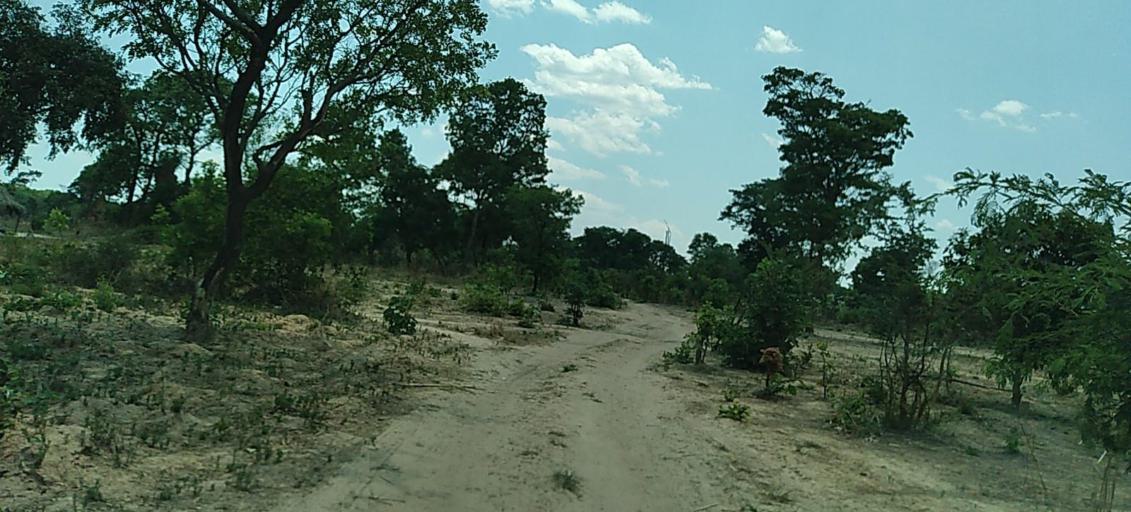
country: ZM
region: Central
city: Kapiri Mposhi
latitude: -13.6336
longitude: 28.7547
